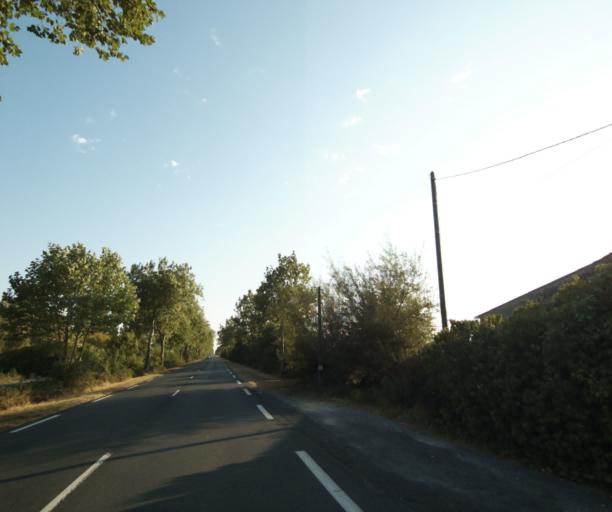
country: FR
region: Poitou-Charentes
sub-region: Departement de la Charente-Maritime
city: Tonnay-Charente
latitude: 45.9645
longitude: -0.9255
